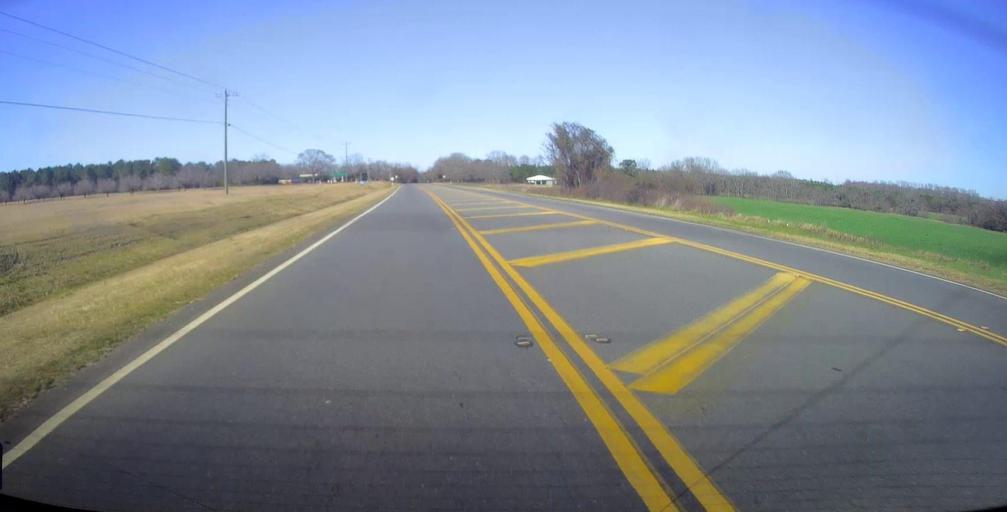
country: US
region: Georgia
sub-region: Macon County
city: Oglethorpe
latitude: 32.2587
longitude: -84.0857
